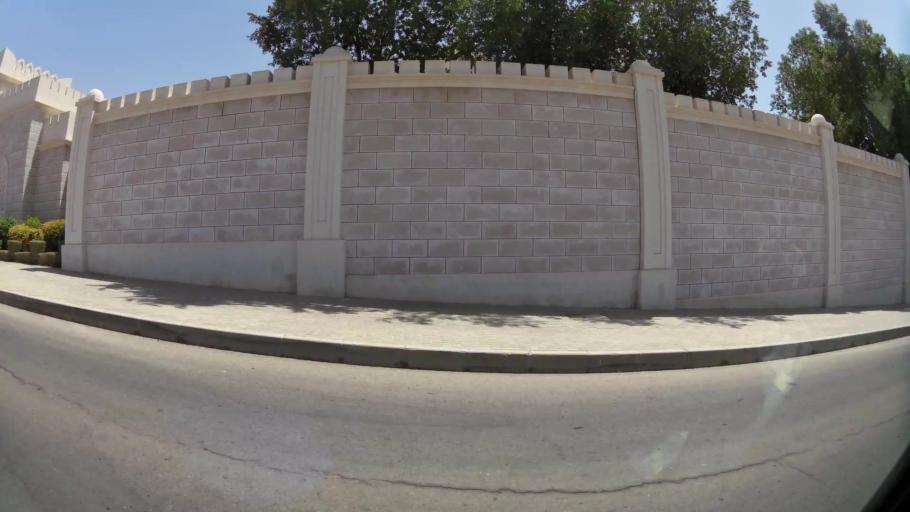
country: OM
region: Muhafazat Masqat
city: Muscat
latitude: 23.6305
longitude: 58.4876
